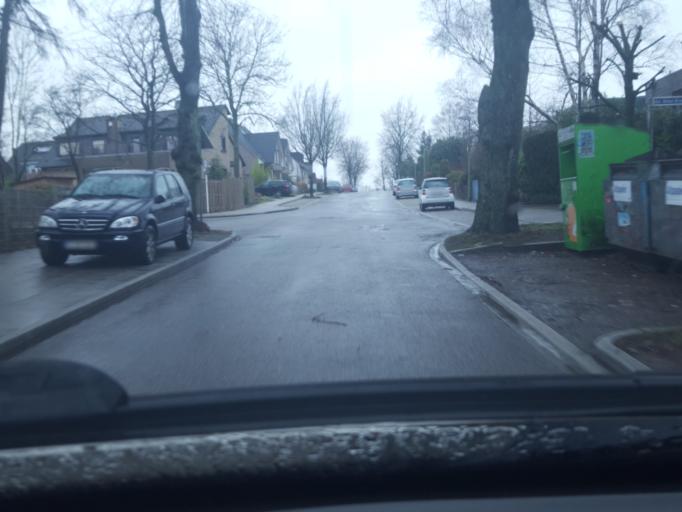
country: DE
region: North Rhine-Westphalia
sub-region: Regierungsbezirk Dusseldorf
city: Velbert
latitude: 51.3927
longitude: 7.0250
